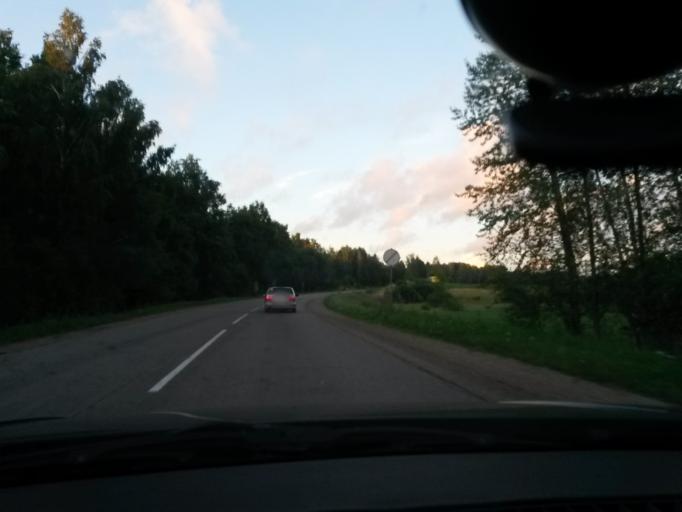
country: LV
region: Madonas Rajons
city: Madona
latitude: 56.8053
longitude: 26.0451
